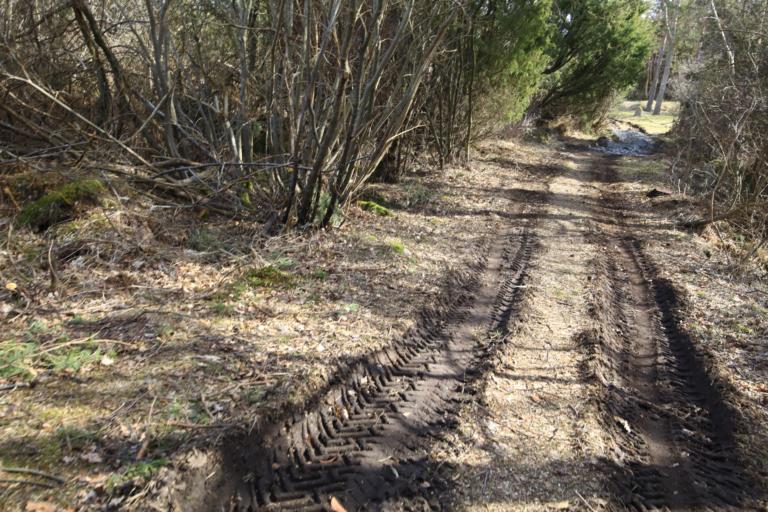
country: SE
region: Halland
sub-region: Kungsbacka Kommun
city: Frillesas
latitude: 57.2710
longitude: 12.1150
